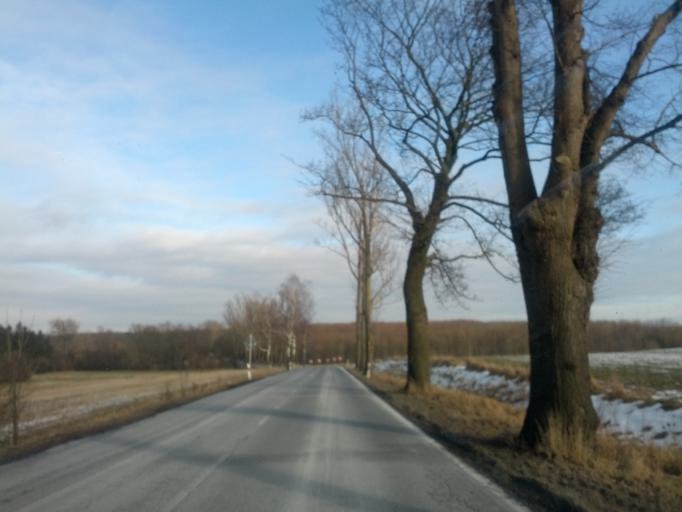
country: DE
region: Thuringia
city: Schonstedt
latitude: 51.0783
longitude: 10.5999
